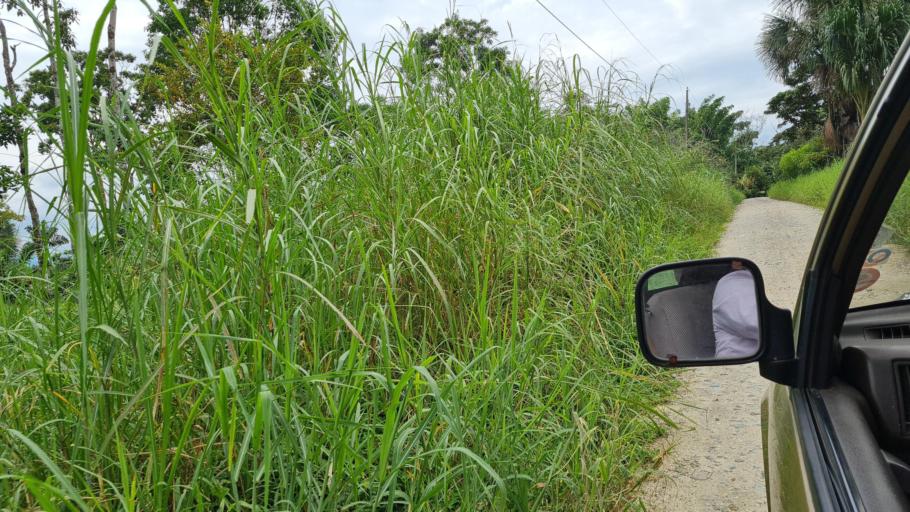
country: EC
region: Napo
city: Tena
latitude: -0.9989
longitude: -77.7558
